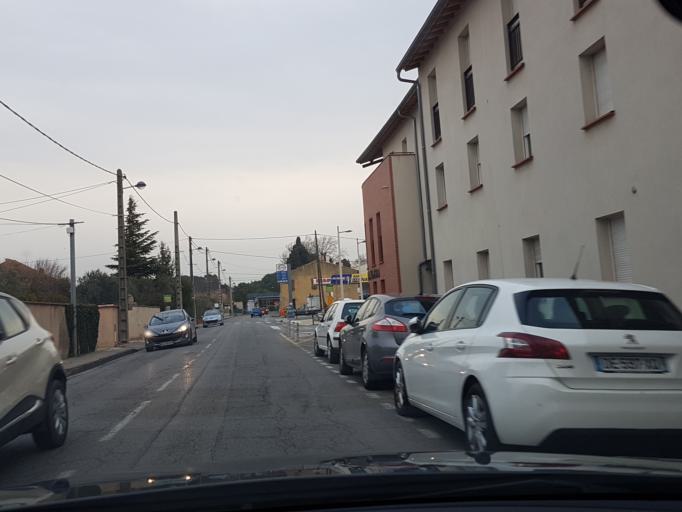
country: FR
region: Provence-Alpes-Cote d'Azur
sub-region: Departement du Vaucluse
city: Monteux
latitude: 44.0345
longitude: 5.0016
